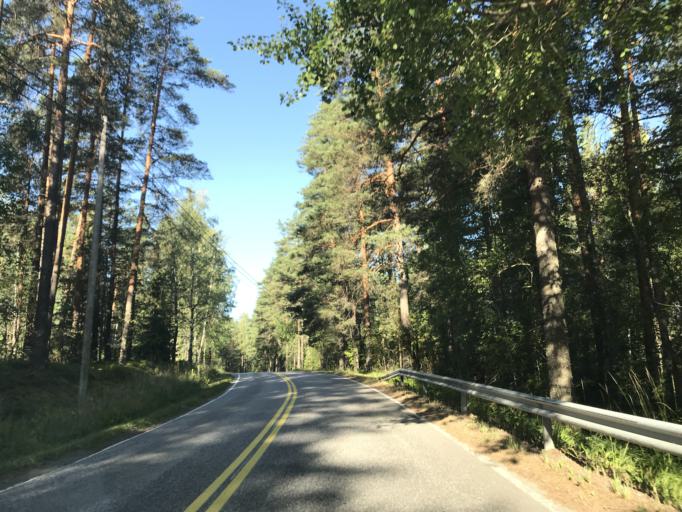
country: FI
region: Uusimaa
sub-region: Helsinki
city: Lohja
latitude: 60.2810
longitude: 24.1338
